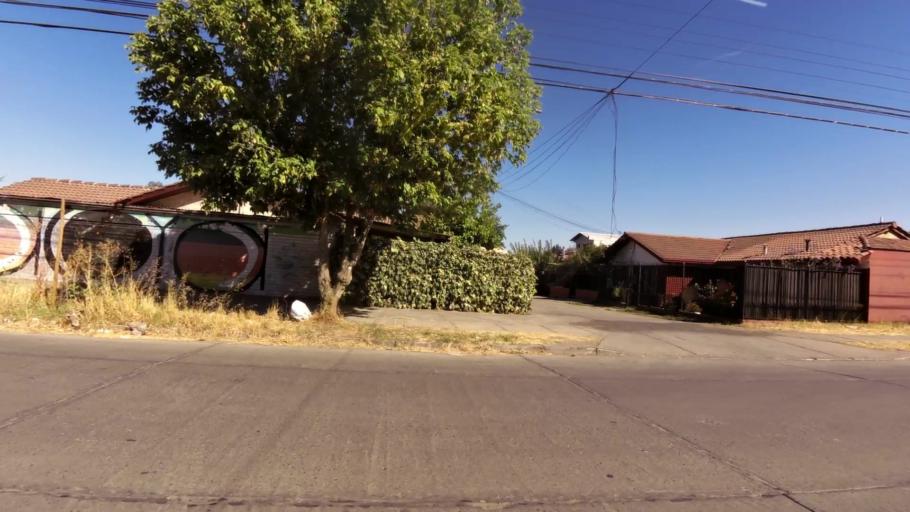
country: CL
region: O'Higgins
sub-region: Provincia de Cachapoal
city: Rancagua
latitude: -34.1810
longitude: -70.7153
